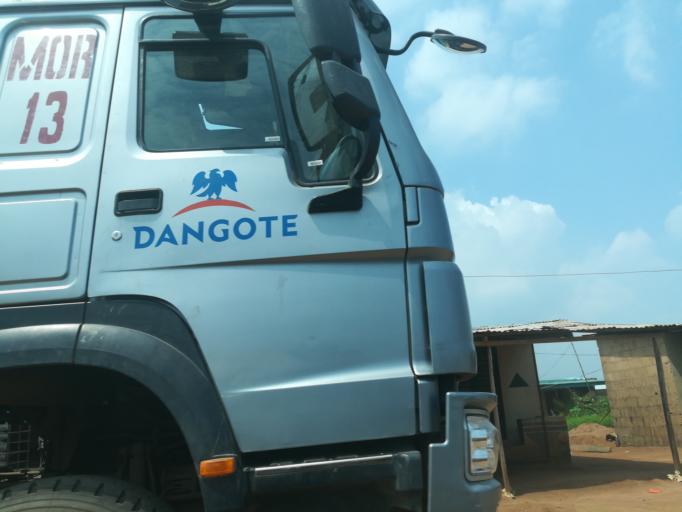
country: NG
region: Lagos
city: Ikorodu
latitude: 6.5926
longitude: 3.6416
